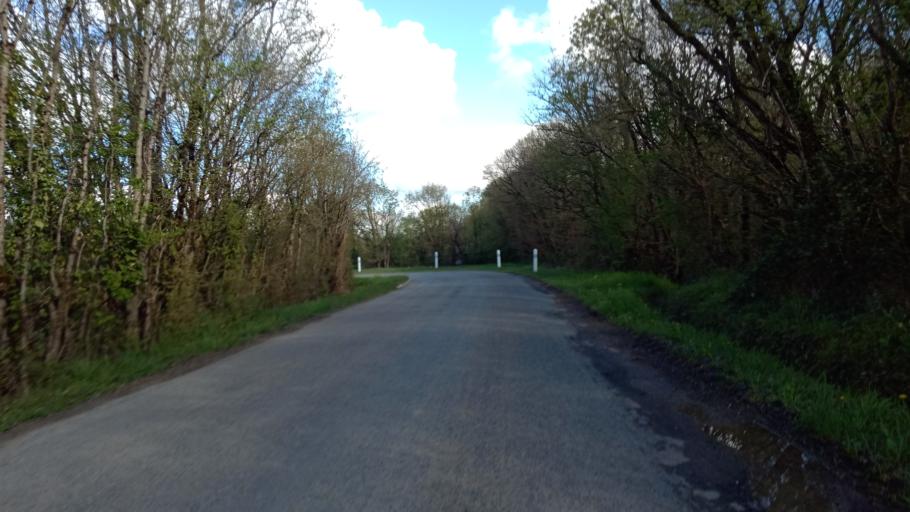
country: FR
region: Poitou-Charentes
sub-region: Departement de la Charente-Maritime
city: Verines
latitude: 46.1479
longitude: -0.9372
